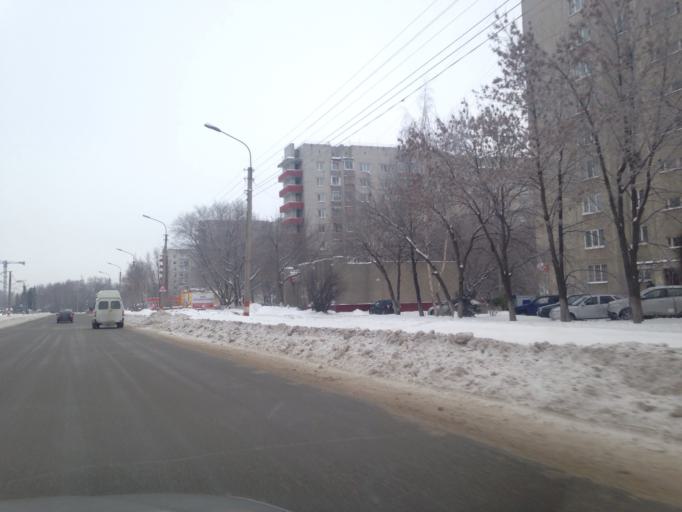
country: RU
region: Ulyanovsk
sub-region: Ulyanovskiy Rayon
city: Ulyanovsk
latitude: 54.3001
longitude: 48.3432
